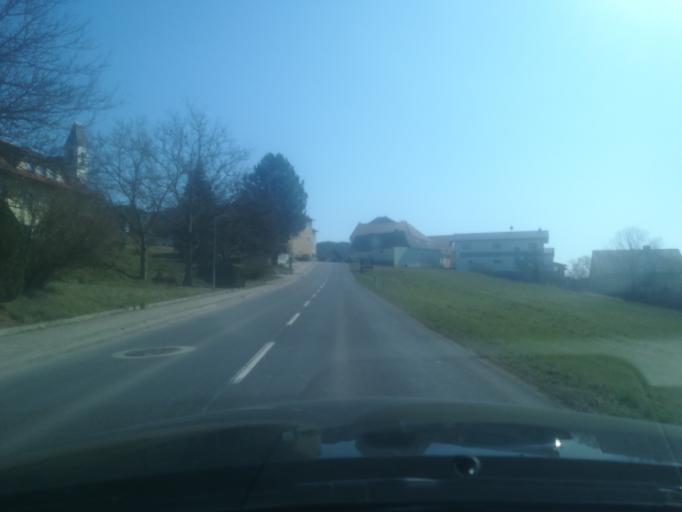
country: AT
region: Upper Austria
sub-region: Politischer Bezirk Freistadt
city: Freistadt
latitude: 48.4440
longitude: 14.5359
